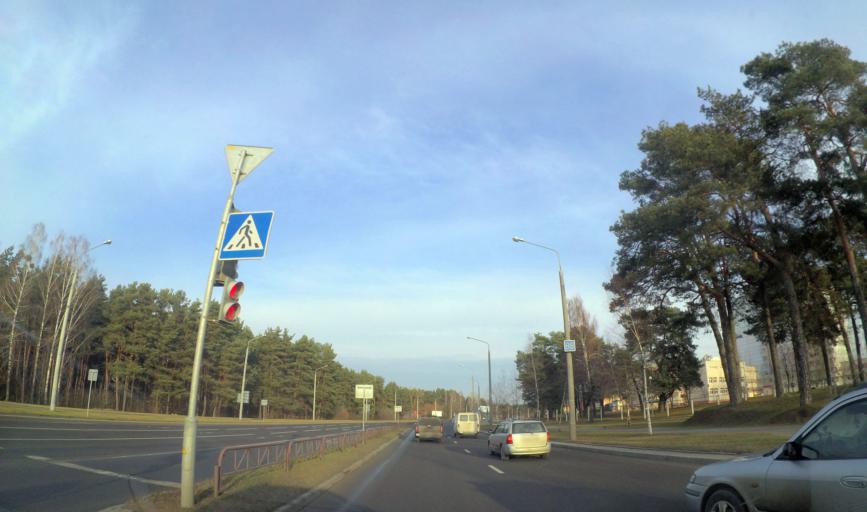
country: BY
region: Grodnenskaya
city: Hrodna
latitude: 53.6733
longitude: 23.7944
